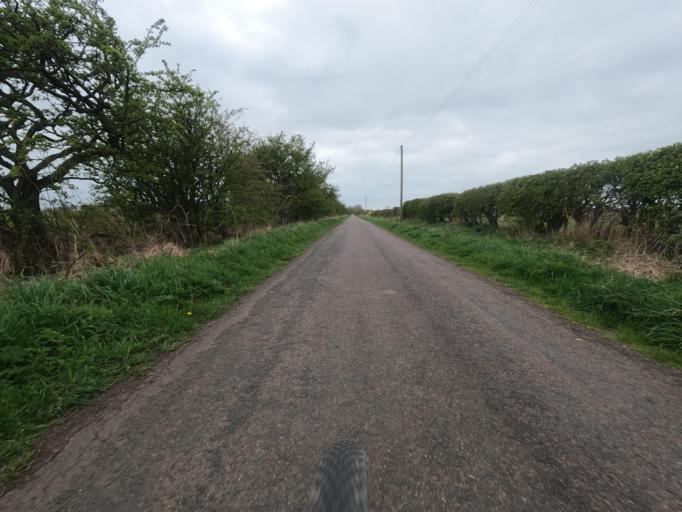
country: GB
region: England
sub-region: Northumberland
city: Ponteland
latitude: 55.0564
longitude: -1.7155
